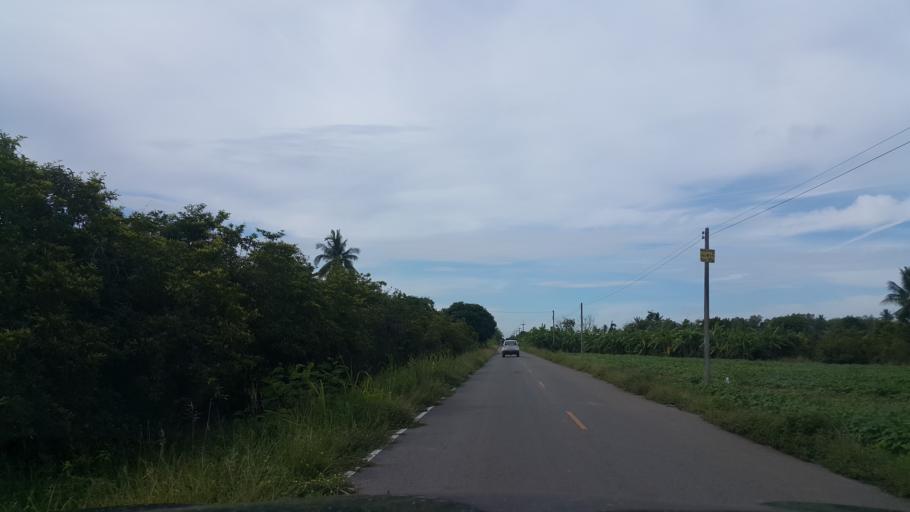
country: TH
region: Sukhothai
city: Sawankhalok
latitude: 17.2733
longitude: 99.9062
